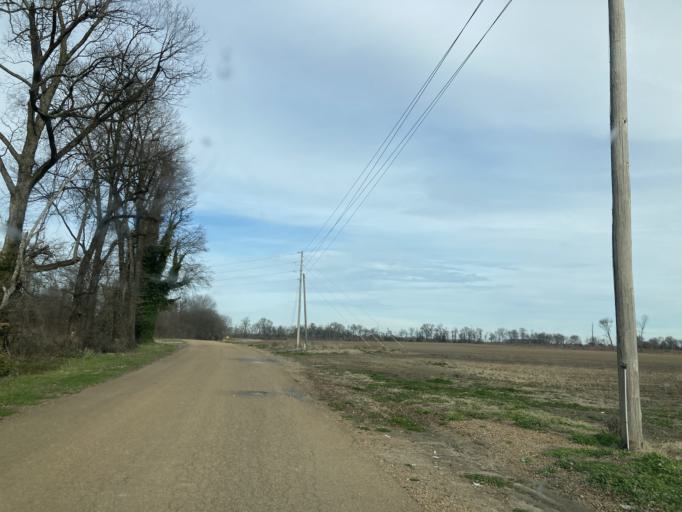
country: US
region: Mississippi
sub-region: Humphreys County
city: Belzoni
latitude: 33.1159
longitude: -90.6131
